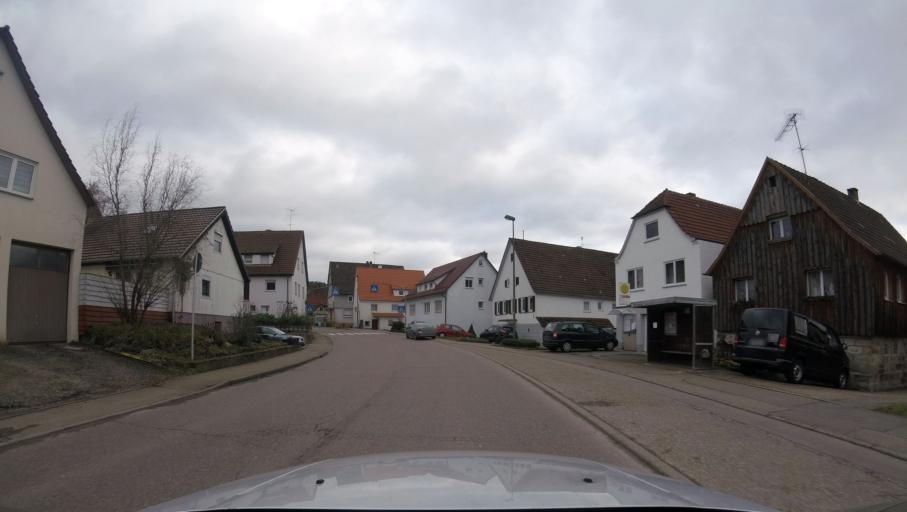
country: DE
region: Baden-Wuerttemberg
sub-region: Regierungsbezirk Stuttgart
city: Rudersberg
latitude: 48.8917
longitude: 9.5414
